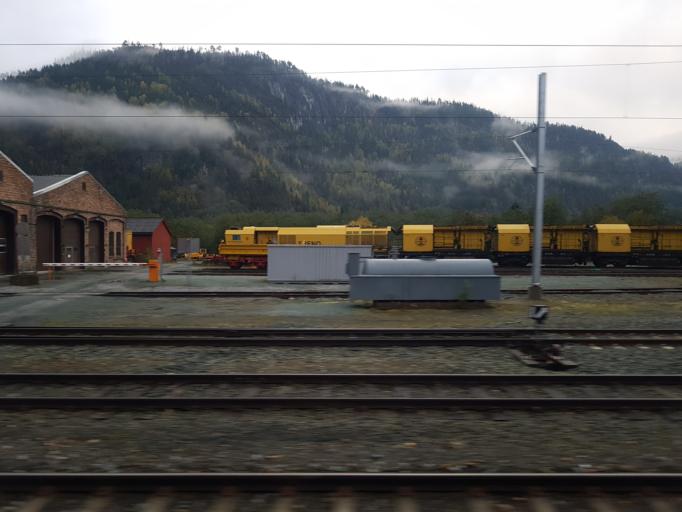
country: NO
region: Sor-Trondelag
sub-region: Midtre Gauldal
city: Storen
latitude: 63.0420
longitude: 10.2824
